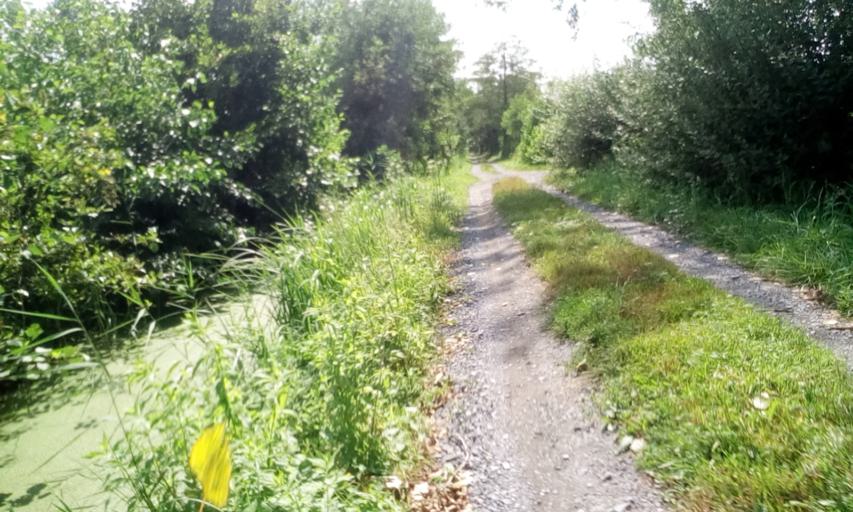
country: FR
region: Lower Normandy
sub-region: Departement du Calvados
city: Bavent
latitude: 49.2353
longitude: -0.1652
